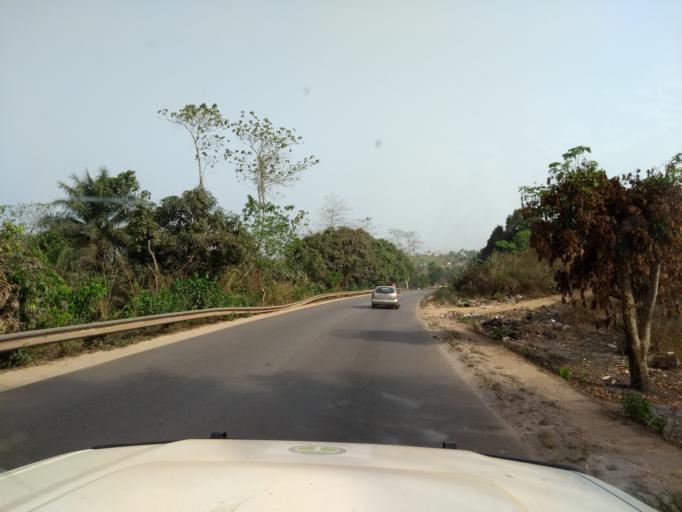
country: GN
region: Kindia
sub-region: Prefecture de Dubreka
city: Dubreka
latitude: 9.8388
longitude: -13.4879
